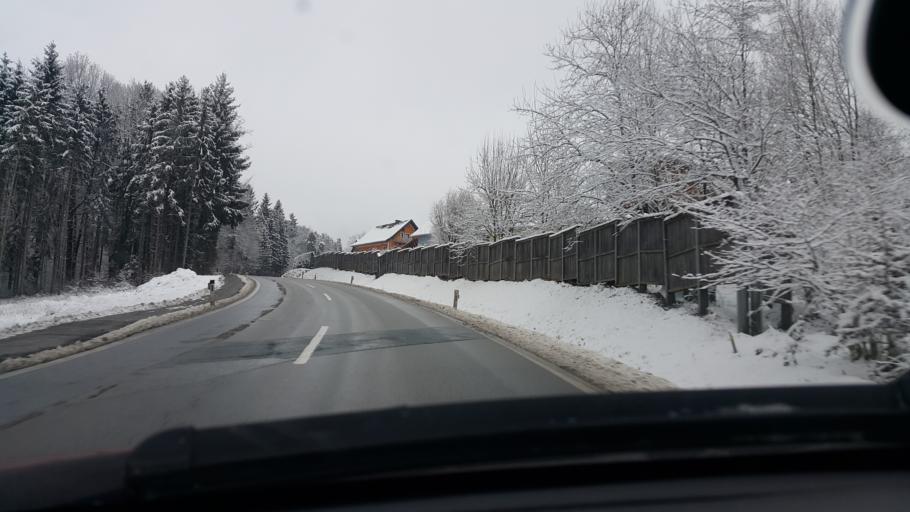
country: AT
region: Styria
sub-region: Politischer Bezirk Graz-Umgebung
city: Hitzendorf
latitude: 47.0223
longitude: 15.2929
